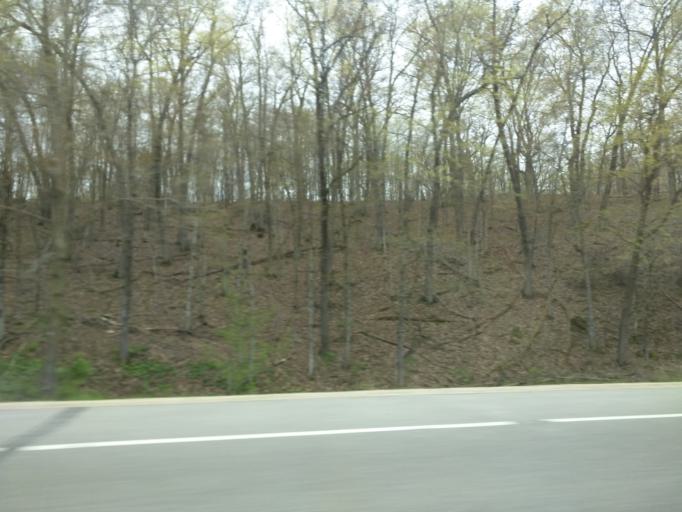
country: US
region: Minnesota
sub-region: Goodhue County
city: Red Wing
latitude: 44.5928
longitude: -92.4165
